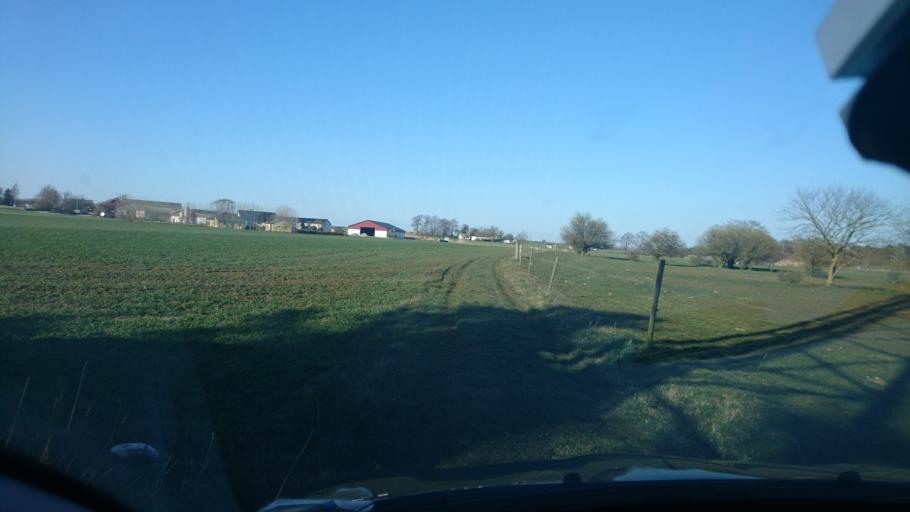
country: SE
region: Skane
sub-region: Simrishamns Kommun
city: Simrishamn
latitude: 55.4218
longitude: 14.2083
